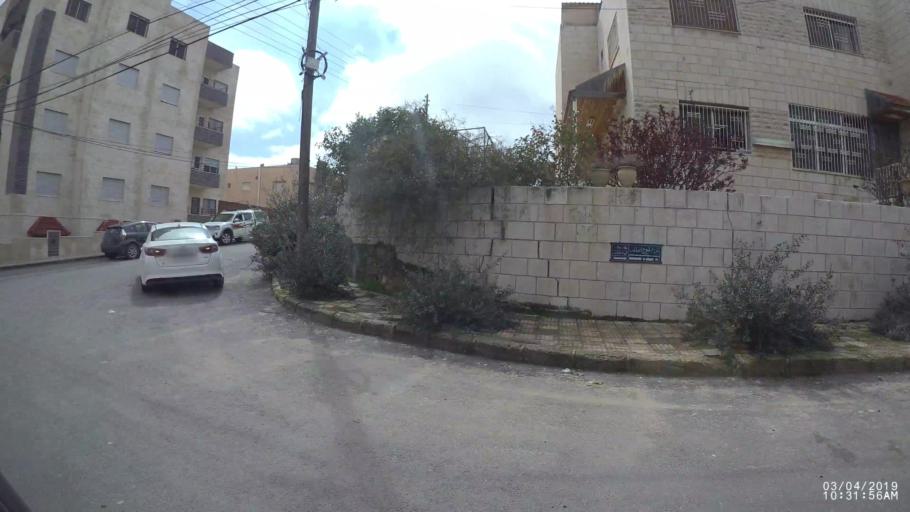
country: JO
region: Amman
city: Wadi as Sir
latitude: 31.9532
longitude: 35.8313
